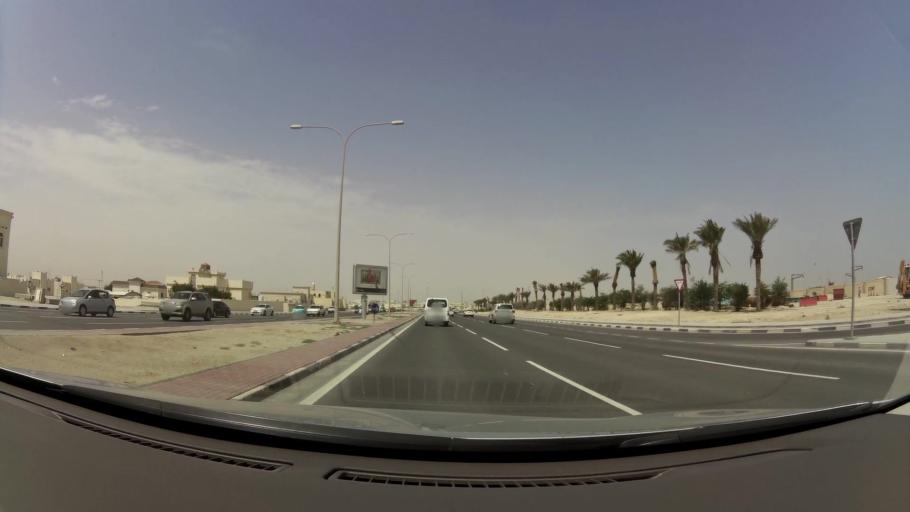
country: QA
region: Baladiyat ar Rayyan
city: Ar Rayyan
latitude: 25.3452
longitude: 51.4799
